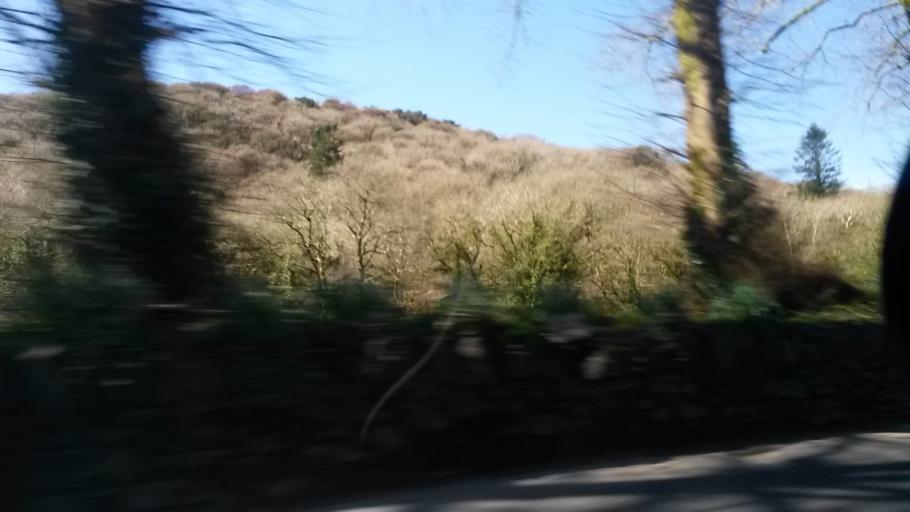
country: IE
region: Munster
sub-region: County Cork
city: Millstreet
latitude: 51.9442
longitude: -9.1652
